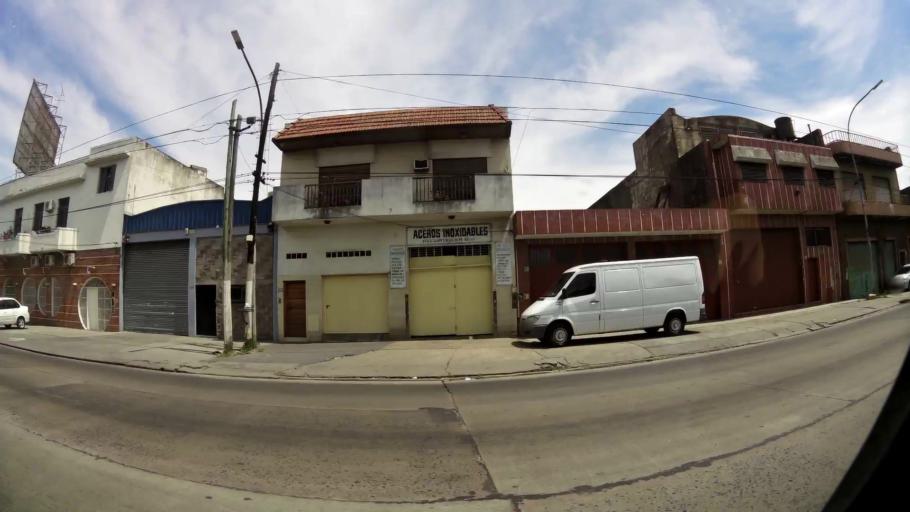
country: AR
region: Buenos Aires
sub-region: Partido de Lanus
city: Lanus
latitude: -34.6759
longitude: -58.4087
